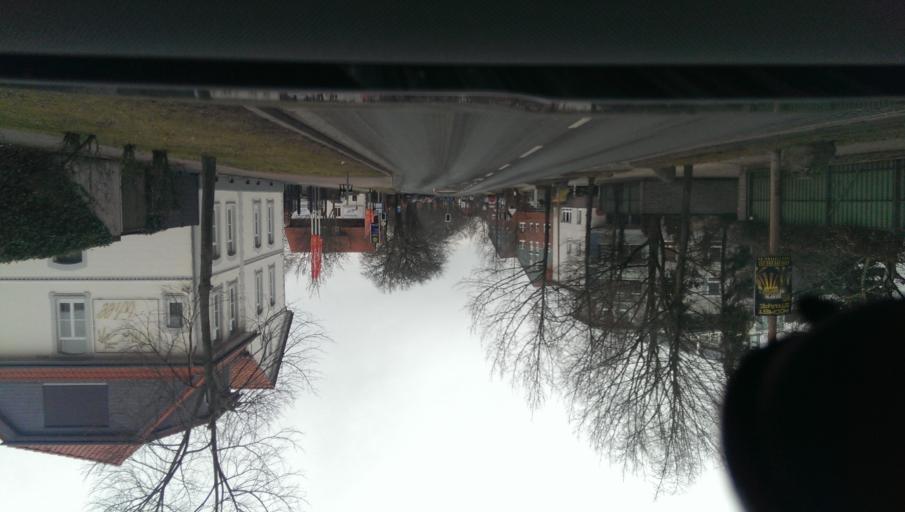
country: DE
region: Lower Saxony
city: Isernhagen Farster Bauerschaft
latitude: 52.4323
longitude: 9.8568
